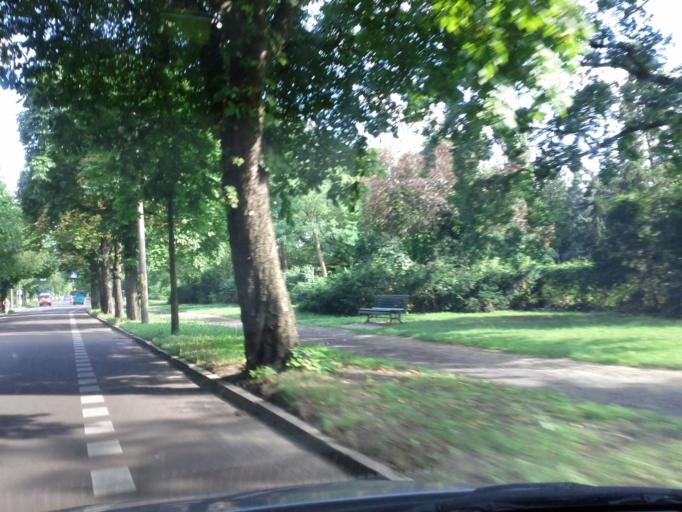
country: DE
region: Berlin
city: Baumschulenweg
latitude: 52.4610
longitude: 13.4936
